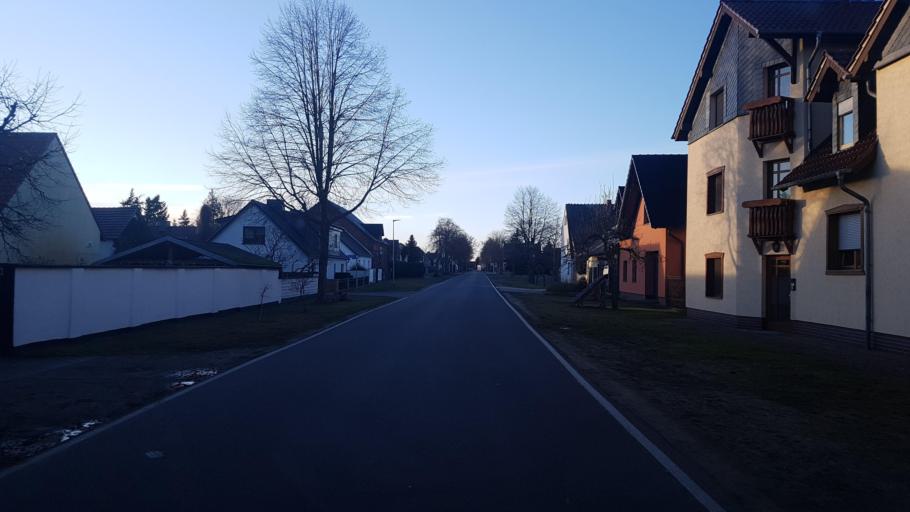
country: DE
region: Brandenburg
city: Drehnow
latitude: 51.8664
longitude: 14.3592
